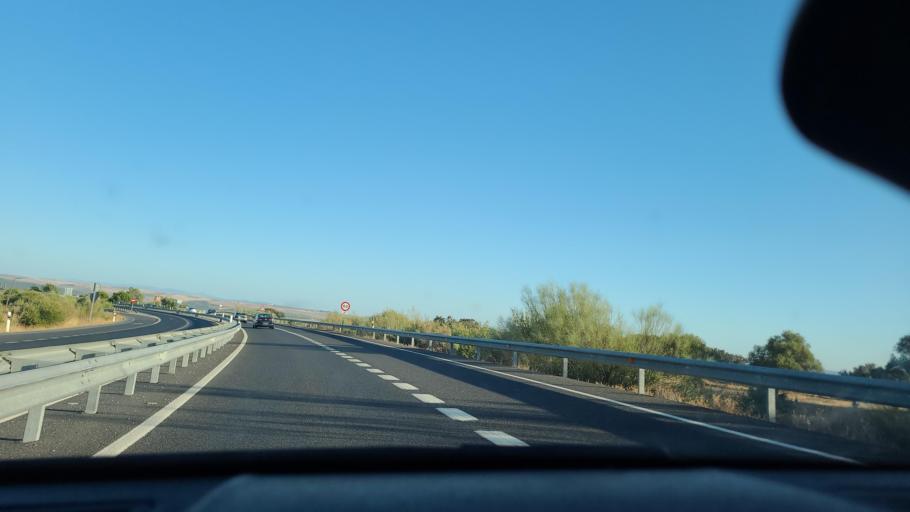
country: ES
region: Andalusia
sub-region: Province of Cordoba
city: Cordoba
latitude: 37.9216
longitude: -4.7649
